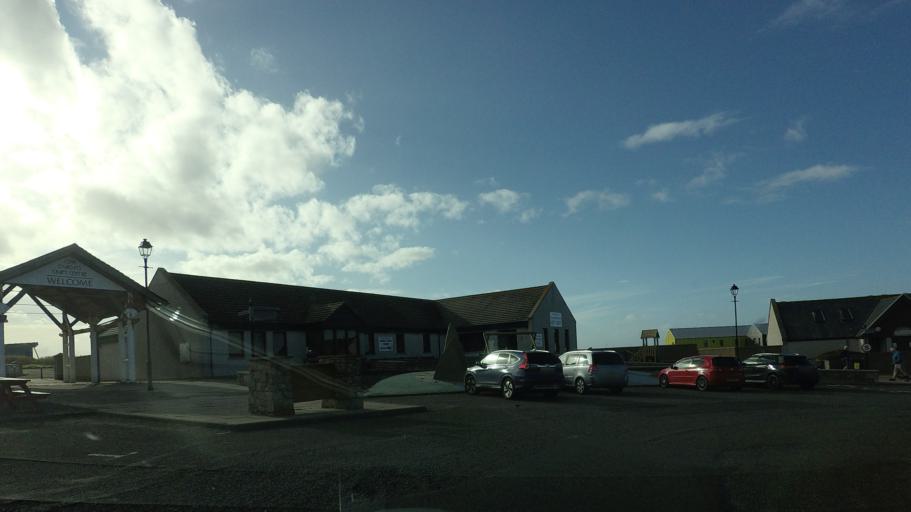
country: GB
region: Scotland
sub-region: Highland
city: Wick
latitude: 58.6430
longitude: -3.0699
